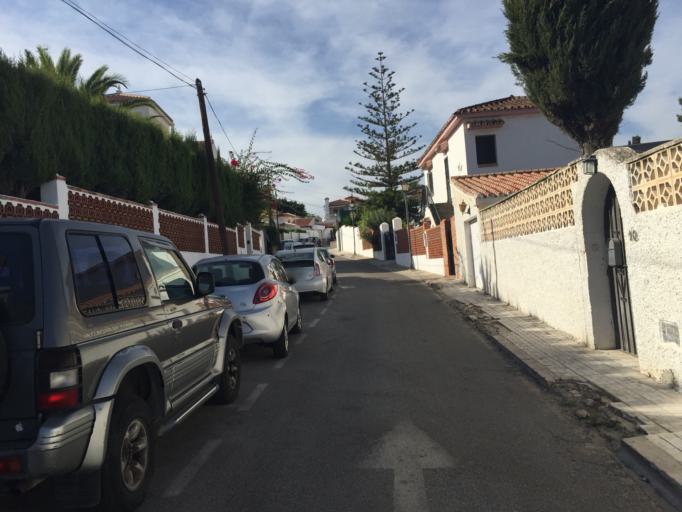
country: ES
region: Andalusia
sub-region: Provincia de Malaga
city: Nerja
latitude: 36.7531
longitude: -3.8717
